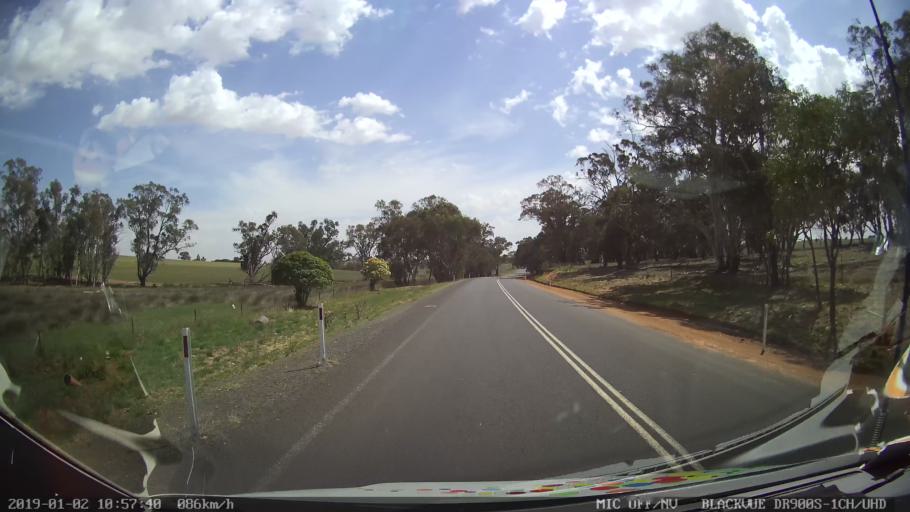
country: AU
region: New South Wales
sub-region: Cootamundra
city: Cootamundra
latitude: -34.6326
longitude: 148.2843
